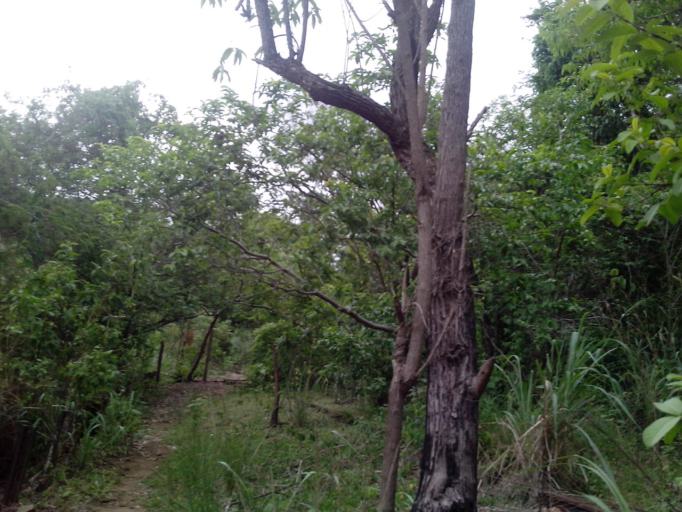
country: BR
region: Rio de Janeiro
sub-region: Miguel Pereira
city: Miguel Pereira
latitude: -22.5090
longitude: -43.5163
